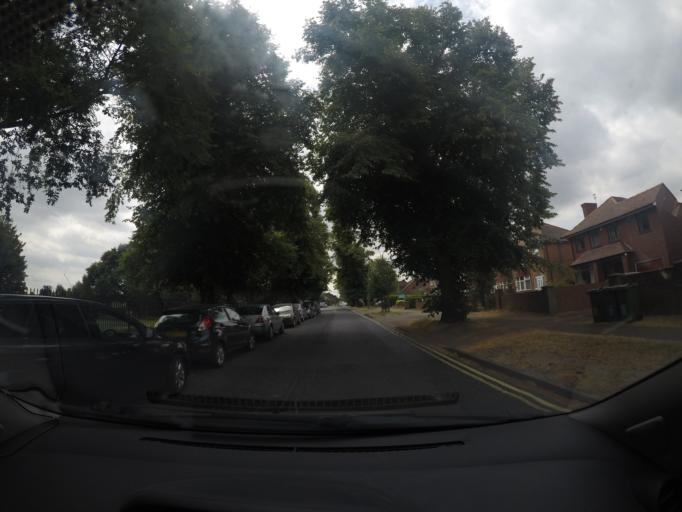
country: GB
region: England
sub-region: City of York
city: Heslington
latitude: 53.9556
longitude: -1.0590
